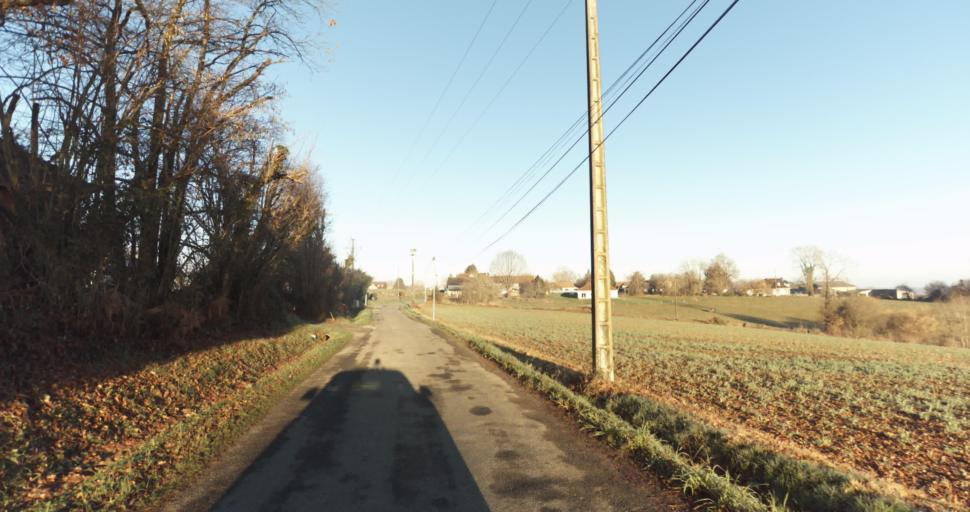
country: FR
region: Aquitaine
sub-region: Departement des Pyrenees-Atlantiques
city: Morlaas
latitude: 43.3323
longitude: -0.2690
